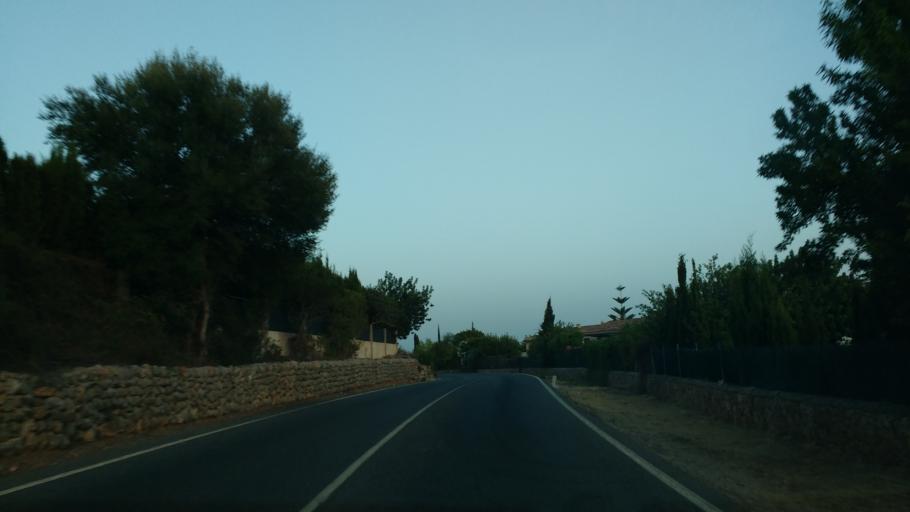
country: ES
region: Balearic Islands
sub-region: Illes Balears
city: Bunyola
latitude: 39.6669
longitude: 2.6877
